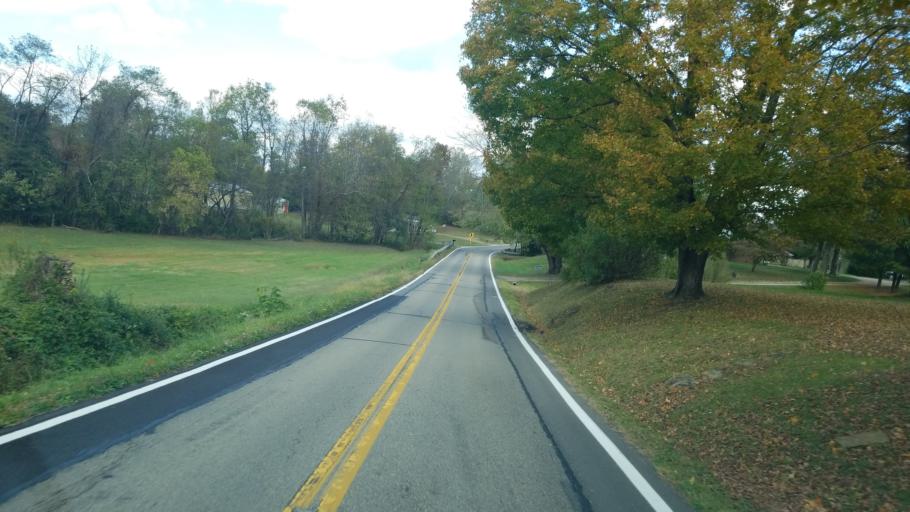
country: US
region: Ohio
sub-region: Jackson County
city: Wellston
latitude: 39.0989
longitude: -82.5785
